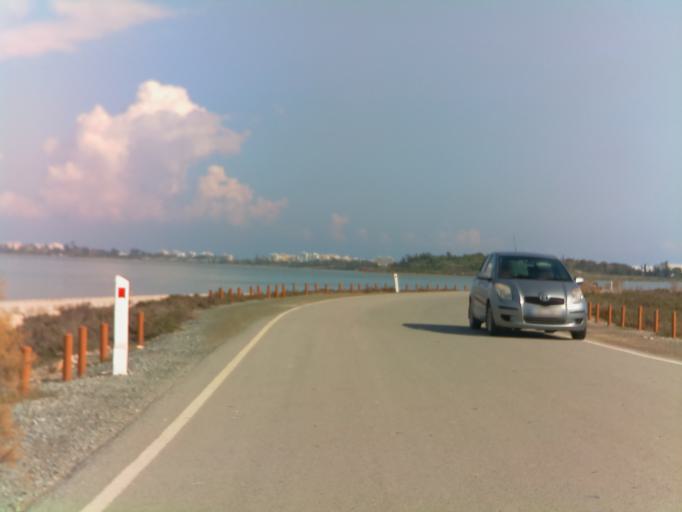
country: CY
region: Larnaka
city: Dhromolaxia
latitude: 34.8819
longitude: 33.6135
